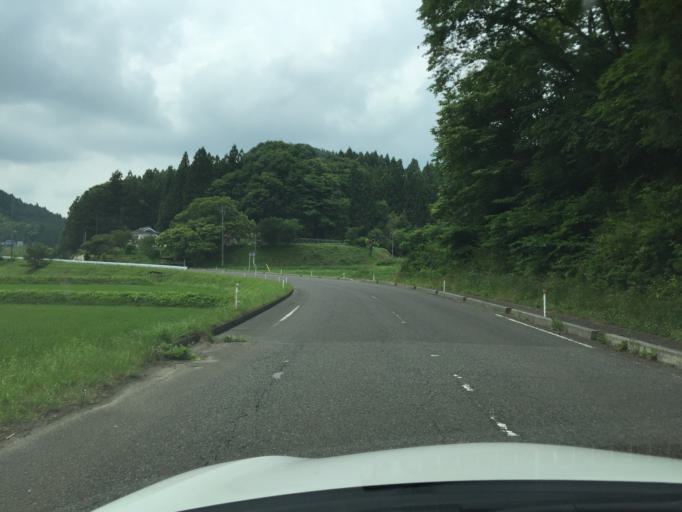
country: JP
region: Fukushima
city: Funehikimachi-funehiki
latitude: 37.2985
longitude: 140.5665
